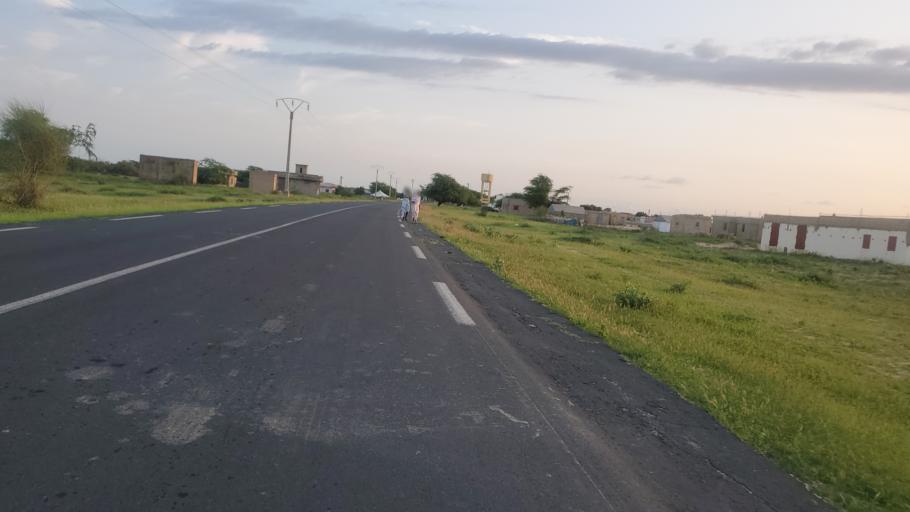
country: SN
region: Saint-Louis
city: Saint-Louis
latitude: 16.1394
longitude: -16.4101
